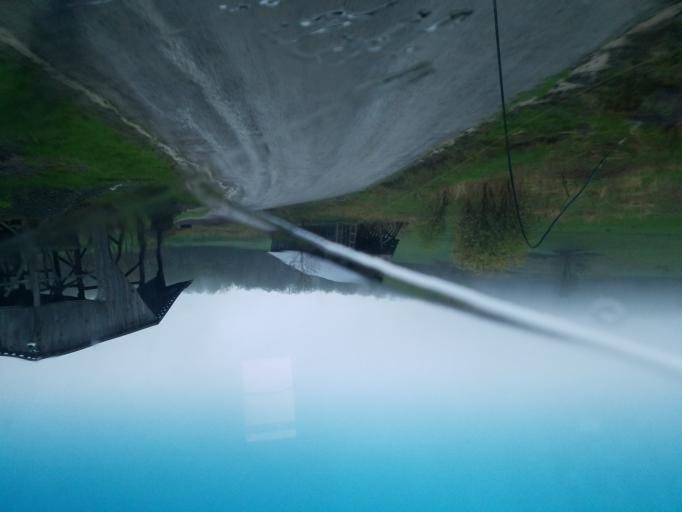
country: US
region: Pennsylvania
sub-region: Tioga County
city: Westfield
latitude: 41.9383
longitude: -77.6938
